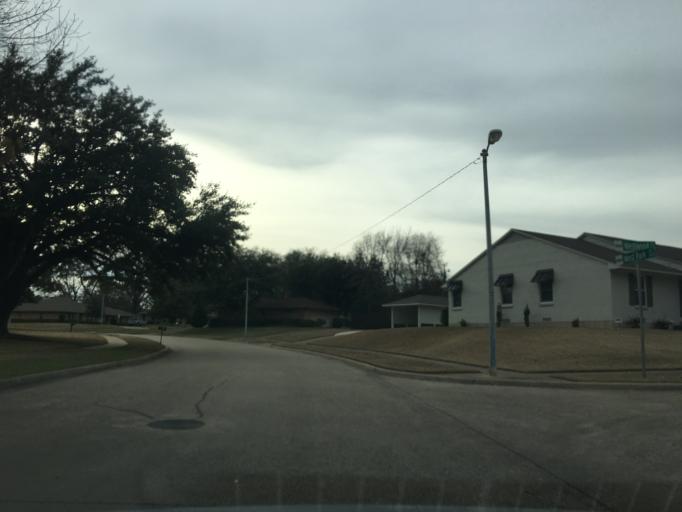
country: US
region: Texas
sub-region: Collin County
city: McKinney
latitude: 33.1964
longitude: -96.6431
